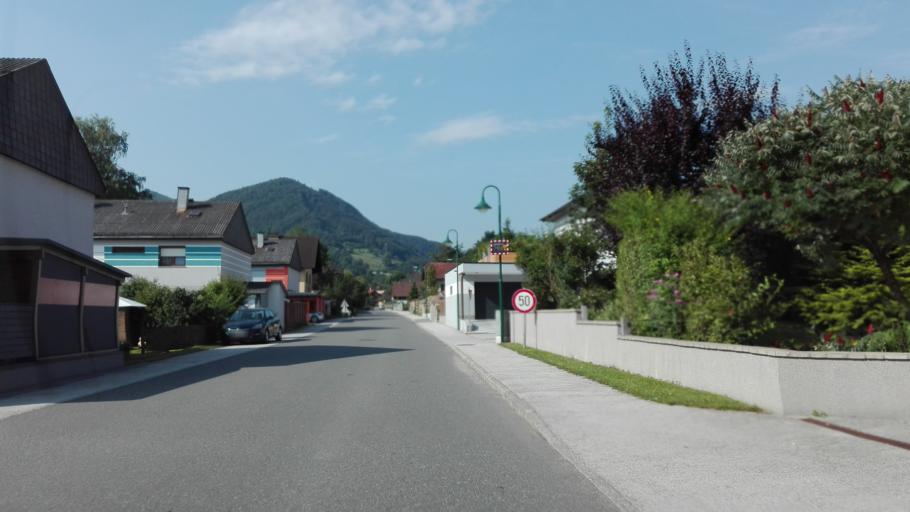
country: AT
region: Lower Austria
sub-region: Politischer Bezirk Lilienfeld
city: Eschenau
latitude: 48.0526
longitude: 15.5707
